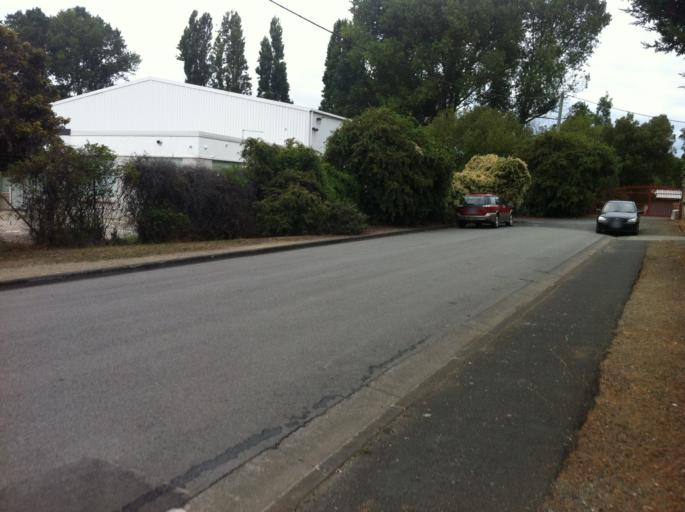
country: AU
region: Tasmania
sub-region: Glenorchy
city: Moonah
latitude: -42.8491
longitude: 147.3022
